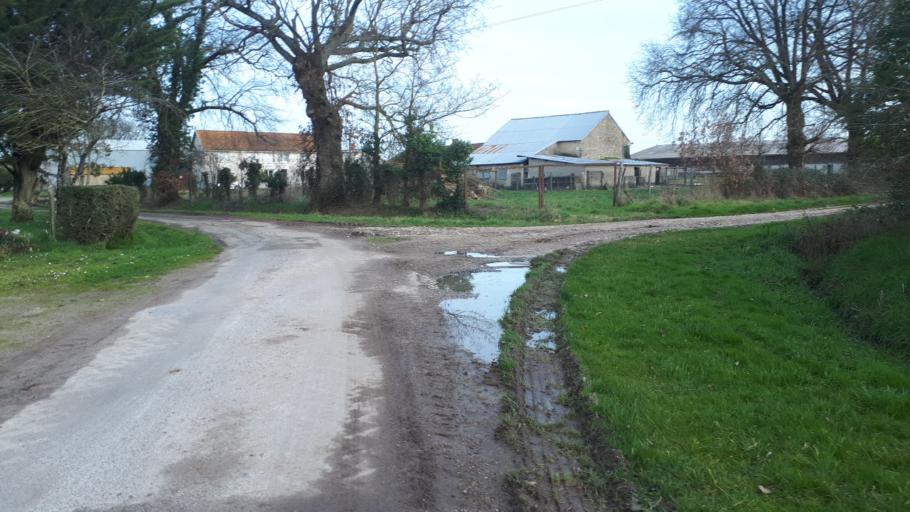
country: FR
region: Poitou-Charentes
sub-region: Departement de la Vienne
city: Archigny
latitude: 46.6199
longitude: 0.7518
